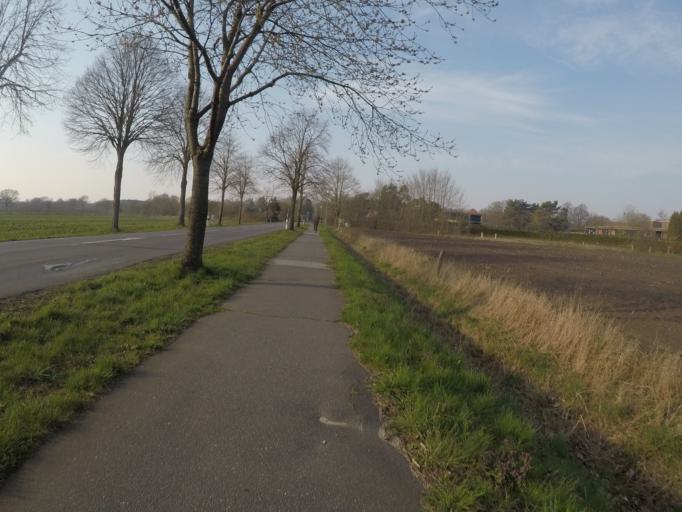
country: DE
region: Schleswig-Holstein
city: Rickling
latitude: 53.9950
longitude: 10.1736
